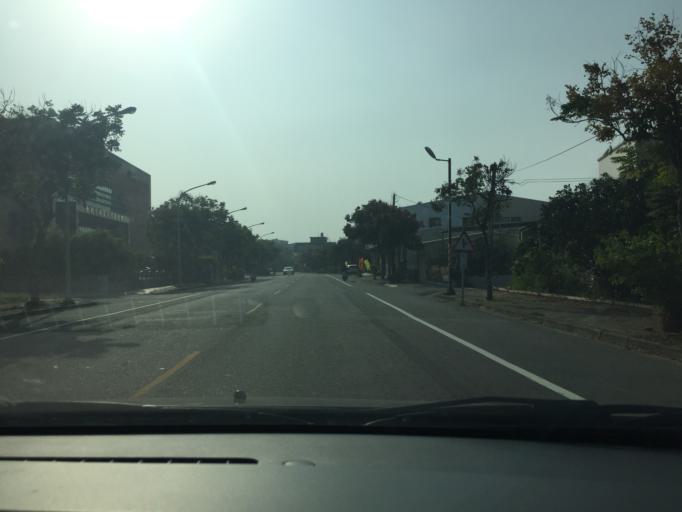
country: TW
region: Taiwan
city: Xinying
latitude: 23.1854
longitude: 120.2594
